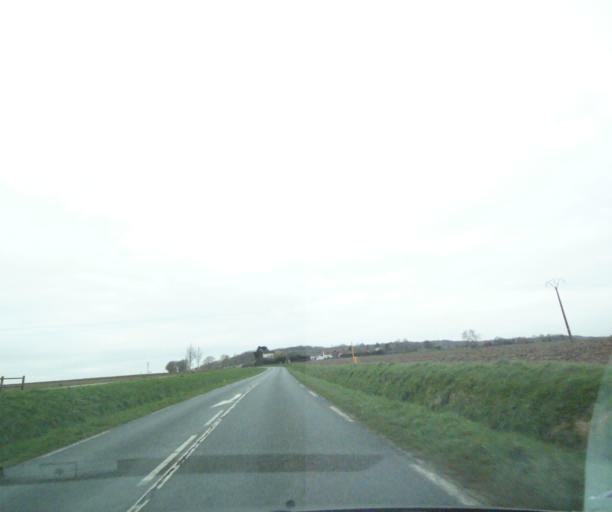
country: FR
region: Picardie
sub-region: Departement de l'Oise
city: Noyon
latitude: 49.5774
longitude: 2.9826
